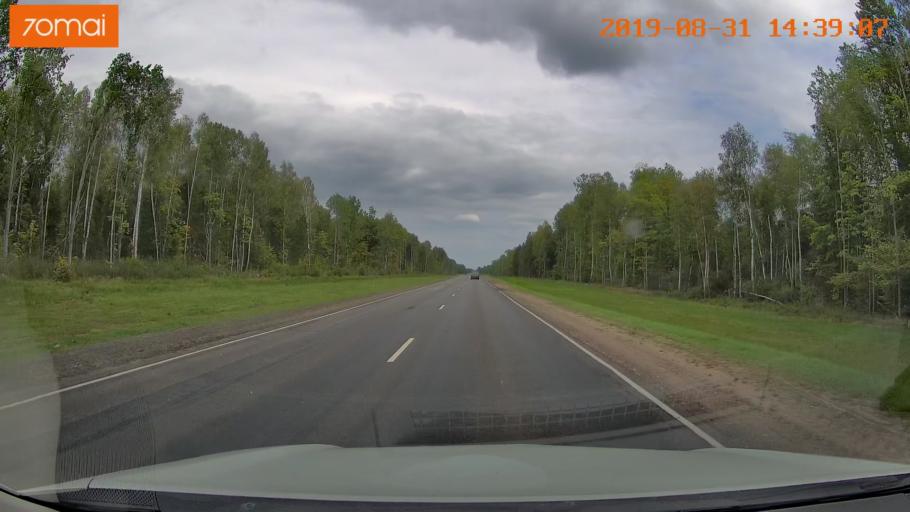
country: RU
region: Smolensk
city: Yekimovichi
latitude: 54.1894
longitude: 33.5450
